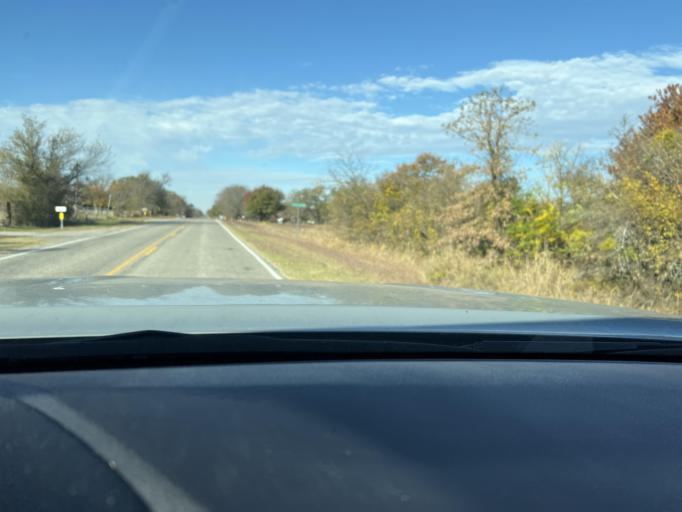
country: US
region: Texas
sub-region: Eastland County
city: Eastland
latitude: 32.4193
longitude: -98.7408
